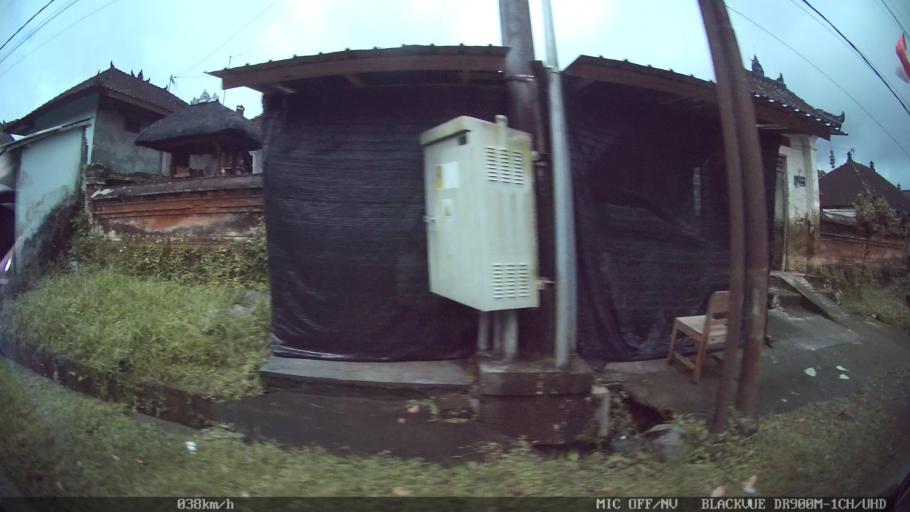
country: ID
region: Bali
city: Pegongan
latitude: -8.4827
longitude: 115.2275
